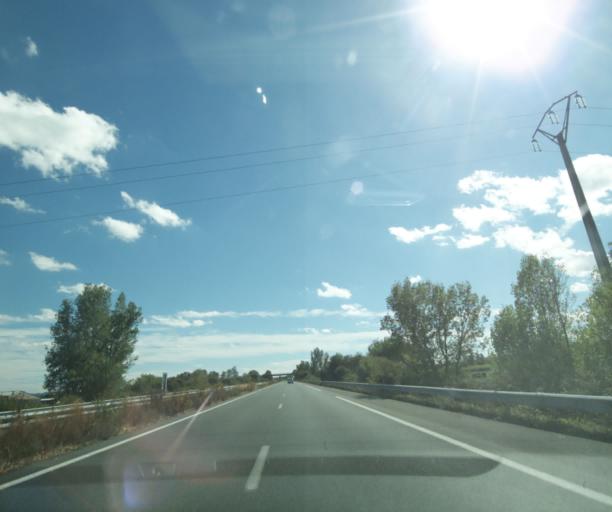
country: FR
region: Aquitaine
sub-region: Departement du Lot-et-Garonne
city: Damazan
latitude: 44.3367
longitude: 0.2537
